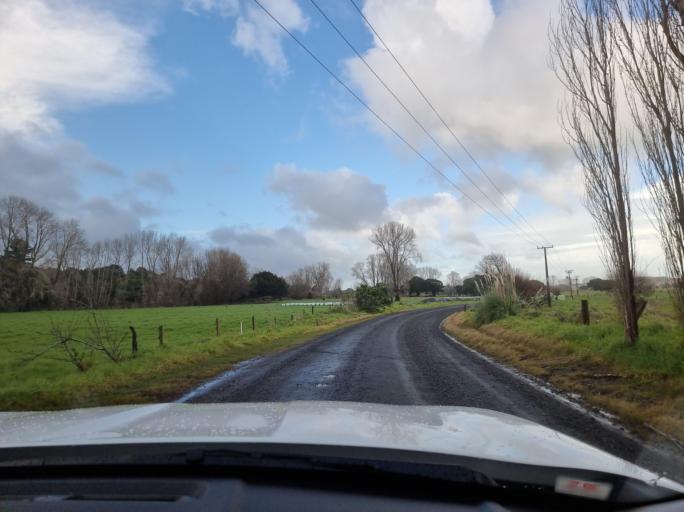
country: NZ
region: Northland
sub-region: Kaipara District
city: Dargaville
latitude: -35.7938
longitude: 173.7253
